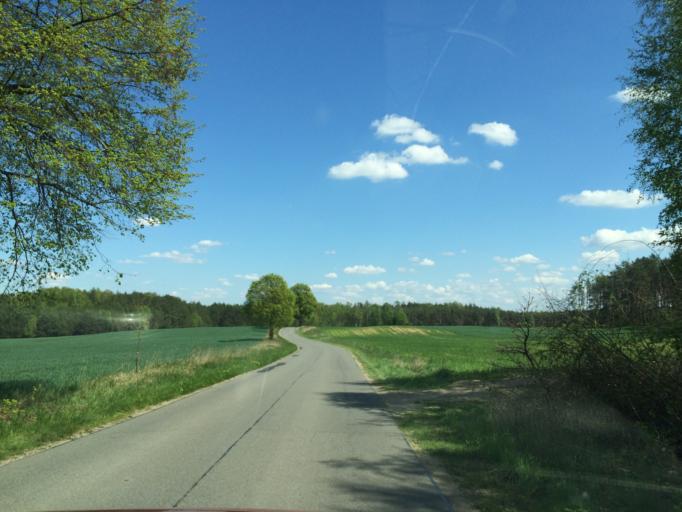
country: PL
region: Warmian-Masurian Voivodeship
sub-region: Powiat ilawski
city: Lubawa
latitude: 53.3879
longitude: 19.7160
